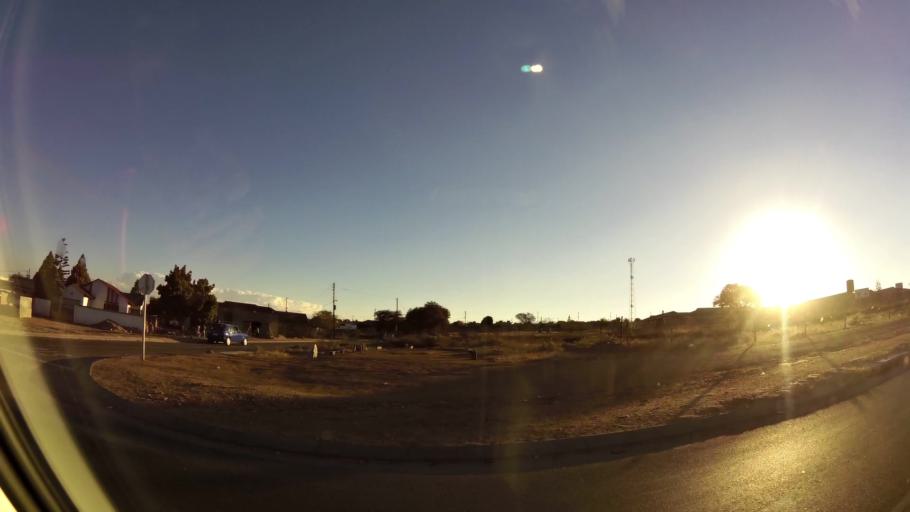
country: ZA
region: Limpopo
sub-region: Capricorn District Municipality
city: Polokwane
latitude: -23.8487
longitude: 29.3546
